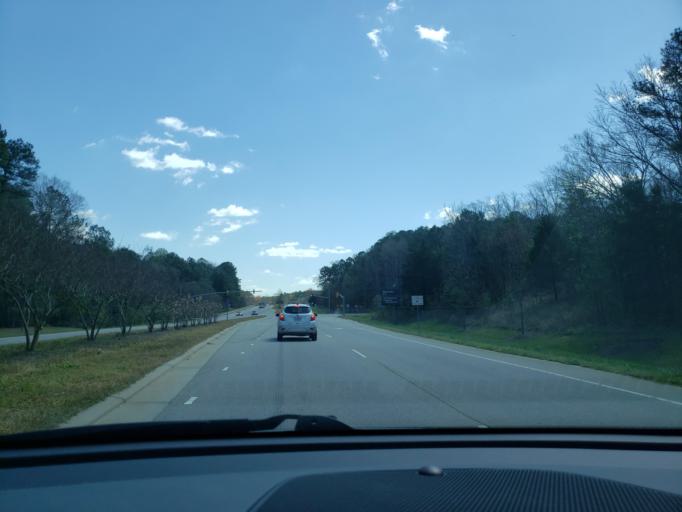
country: US
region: North Carolina
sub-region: Durham County
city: Durham
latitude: 35.9250
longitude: -78.8666
